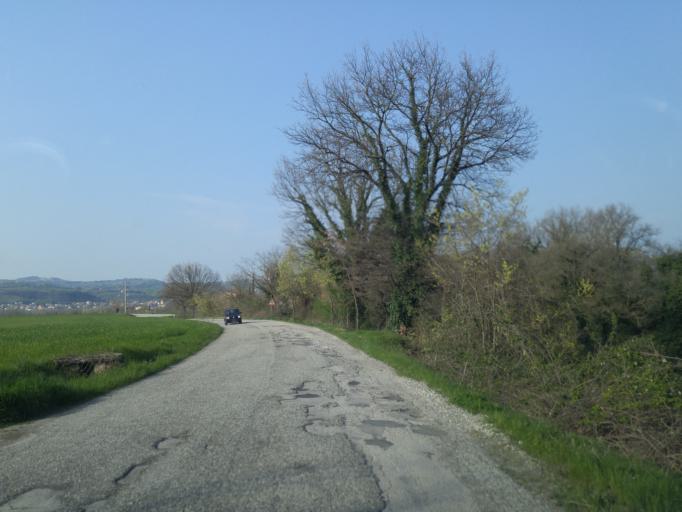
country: IT
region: The Marches
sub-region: Provincia di Pesaro e Urbino
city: Tavernelle
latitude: 43.7079
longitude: 12.8878
